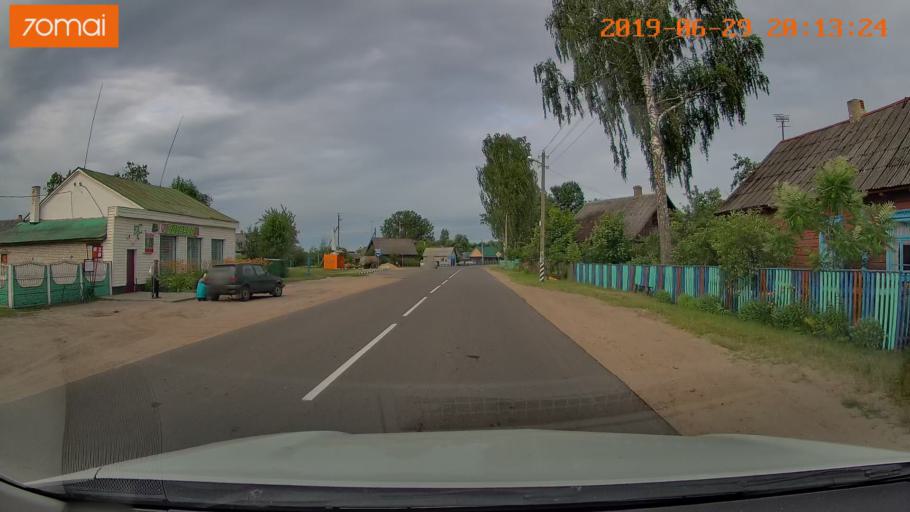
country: BY
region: Brest
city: Lahishyn
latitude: 52.3659
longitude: 26.1455
